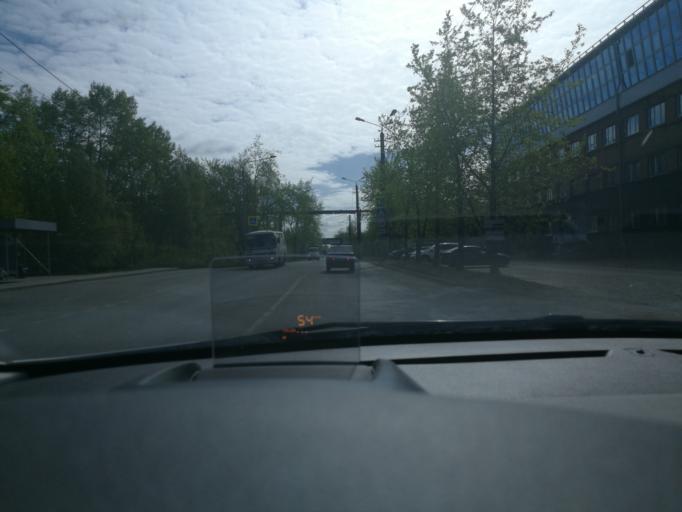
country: RU
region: Arkhangelskaya
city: Arkhangel'sk
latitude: 64.5965
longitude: 40.5667
